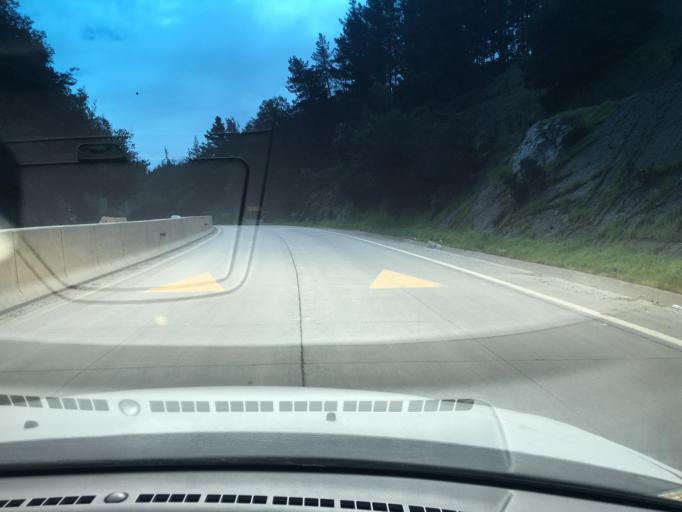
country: CL
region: Valparaiso
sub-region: Provincia de Valparaiso
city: Vina del Mar
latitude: -33.1064
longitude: -71.5575
